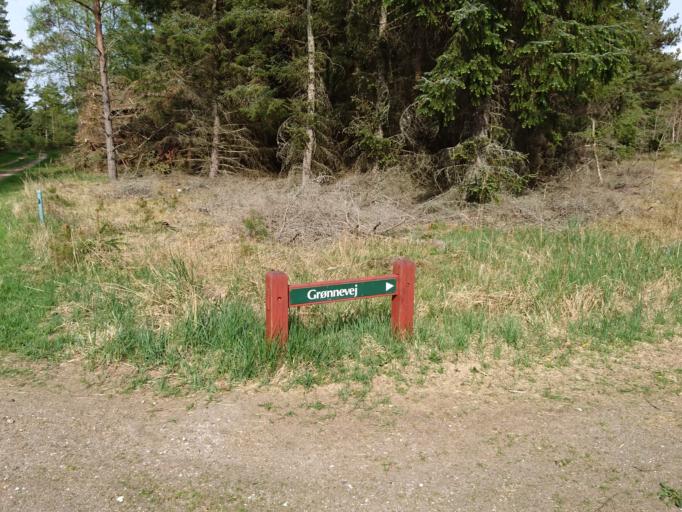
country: DK
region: North Denmark
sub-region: Frederikshavn Kommune
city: Skagen
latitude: 57.7100
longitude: 10.5122
